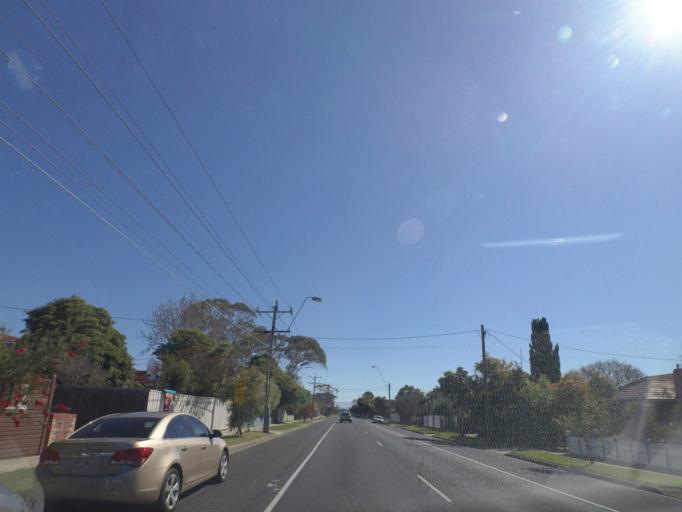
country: AU
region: Victoria
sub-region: Kingston
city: Edithvale
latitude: -38.0360
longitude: 145.1168
